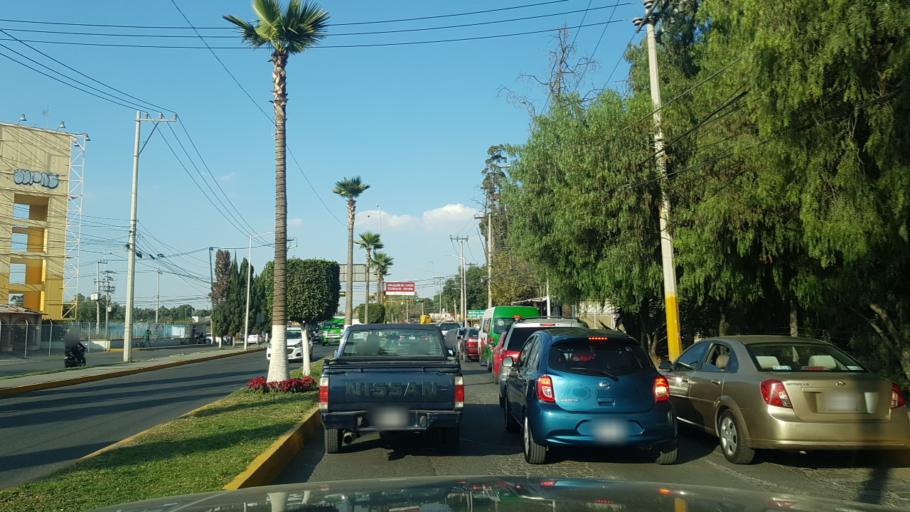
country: MX
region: Mexico
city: Santiago Teyahualco
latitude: 19.6631
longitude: -99.1292
